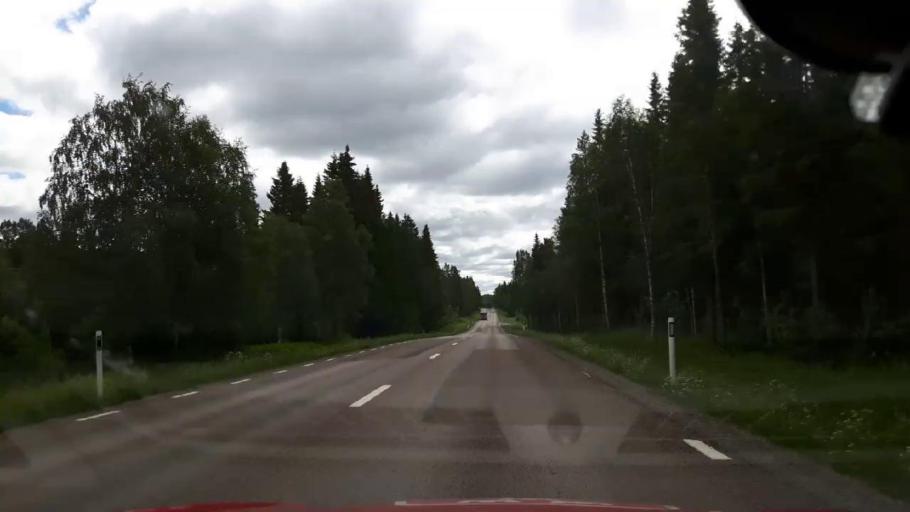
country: SE
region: Jaemtland
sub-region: OEstersunds Kommun
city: Brunflo
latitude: 62.9839
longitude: 14.9947
